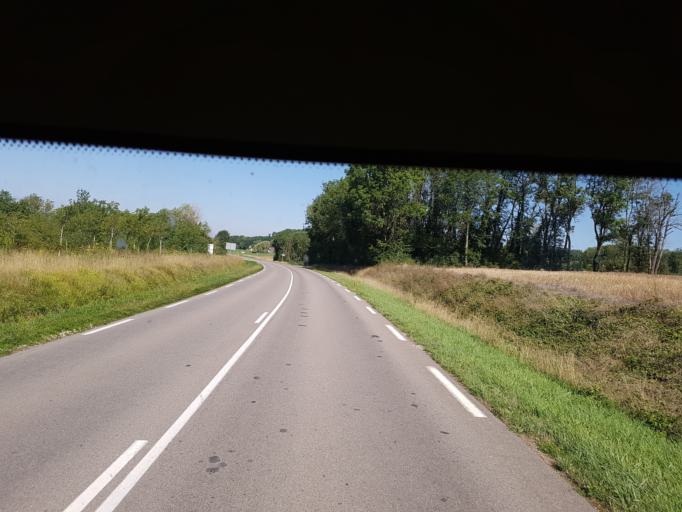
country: FR
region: Franche-Comte
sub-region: Departement du Jura
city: Poligny
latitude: 46.8207
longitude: 5.5797
